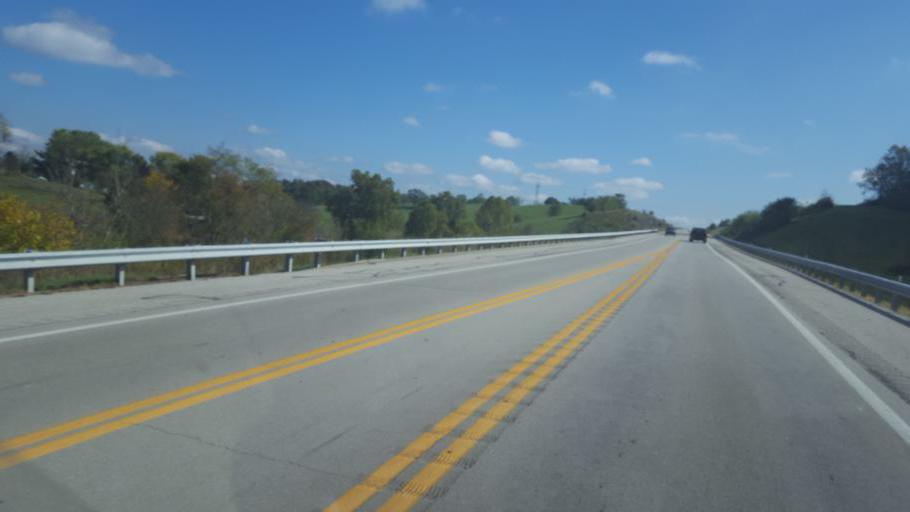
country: US
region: Kentucky
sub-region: Mason County
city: Maysville
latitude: 38.5837
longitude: -83.6963
